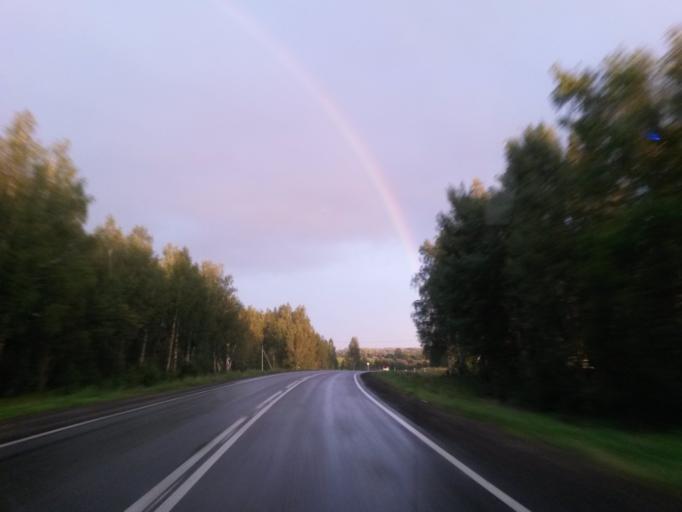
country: RU
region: Jaroslavl
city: Gavrilov-Yam
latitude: 57.3384
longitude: 39.9184
